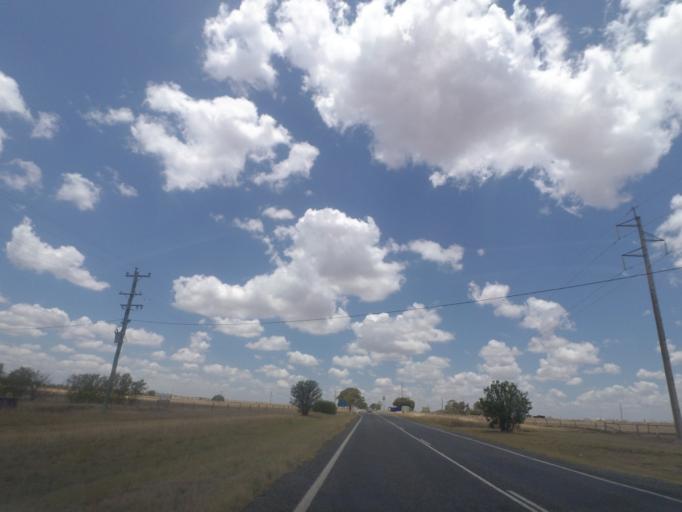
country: AU
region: Queensland
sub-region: Southern Downs
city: Warwick
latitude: -27.9300
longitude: 151.9857
